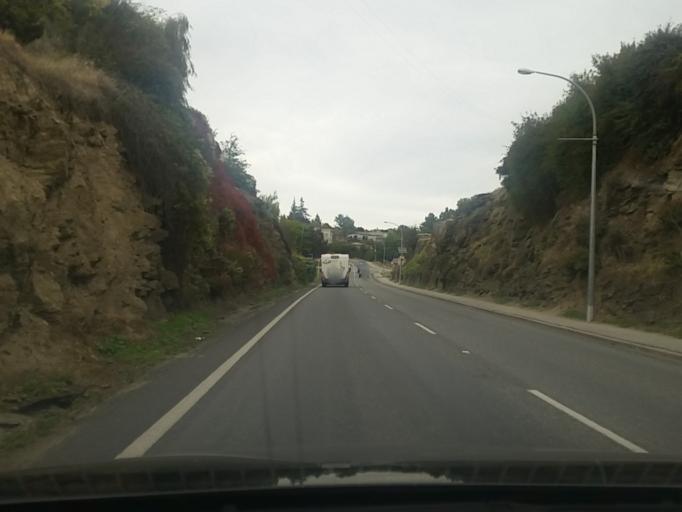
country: NZ
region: Otago
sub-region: Queenstown-Lakes District
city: Wanaka
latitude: -45.2595
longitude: 169.3897
